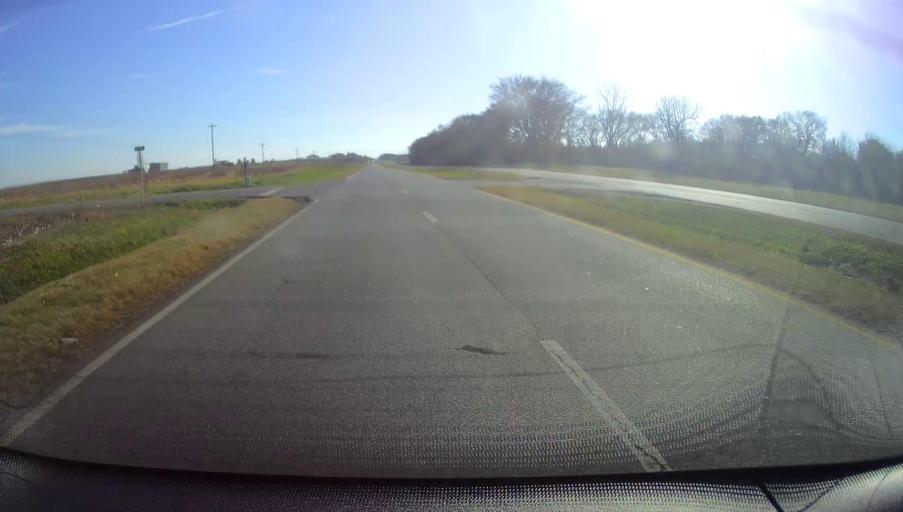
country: US
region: Alabama
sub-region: Morgan County
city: Decatur
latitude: 34.6662
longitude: -86.9500
